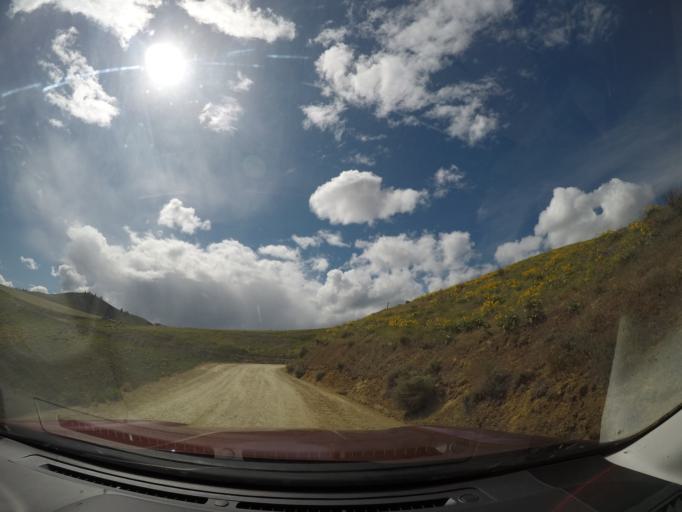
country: US
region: Washington
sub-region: Chelan County
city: West Wenatchee
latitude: 47.4629
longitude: -120.3807
